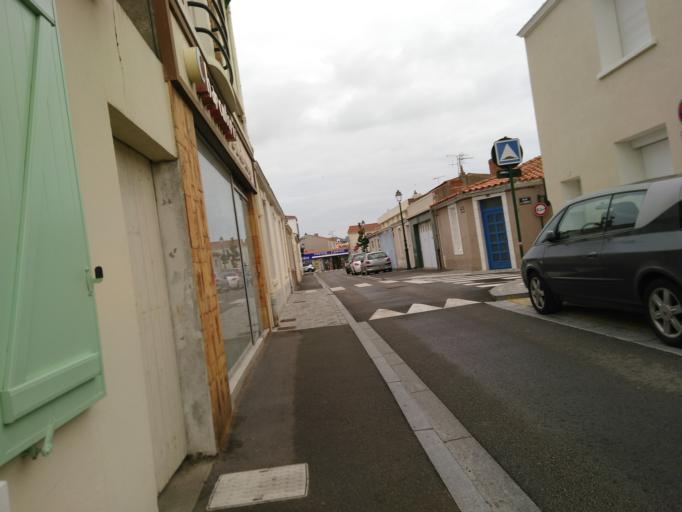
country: FR
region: Pays de la Loire
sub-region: Departement de la Vendee
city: Les Sables-d'Olonne
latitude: 46.4956
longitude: -1.8009
